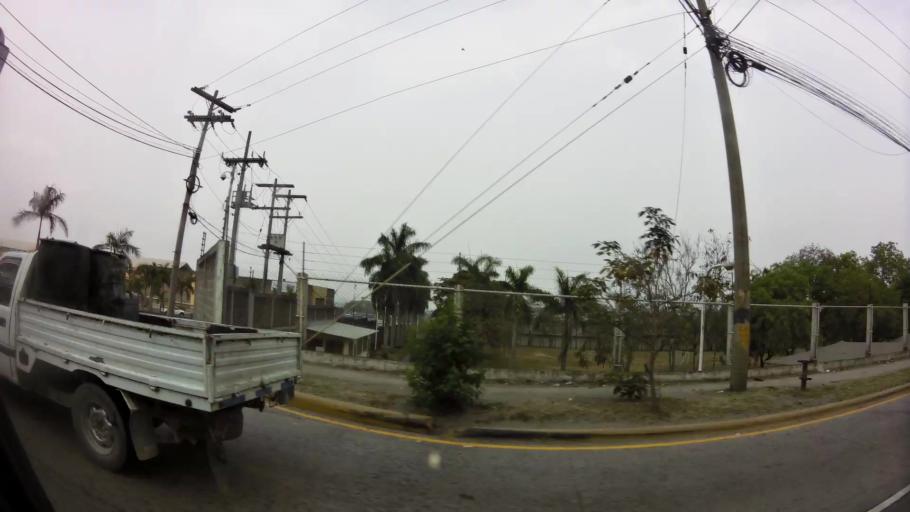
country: HN
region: Cortes
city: Armenta
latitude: 15.4699
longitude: -88.0334
